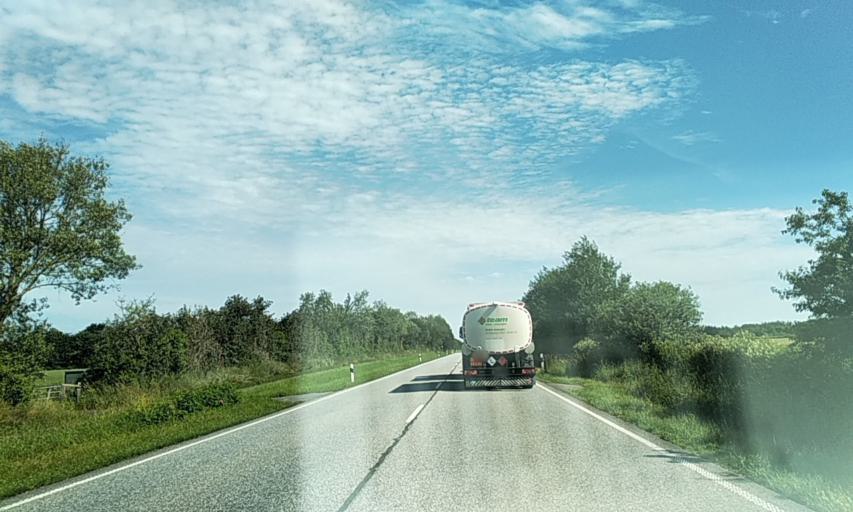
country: DE
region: Schleswig-Holstein
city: Kropp
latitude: 54.4251
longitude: 9.5312
